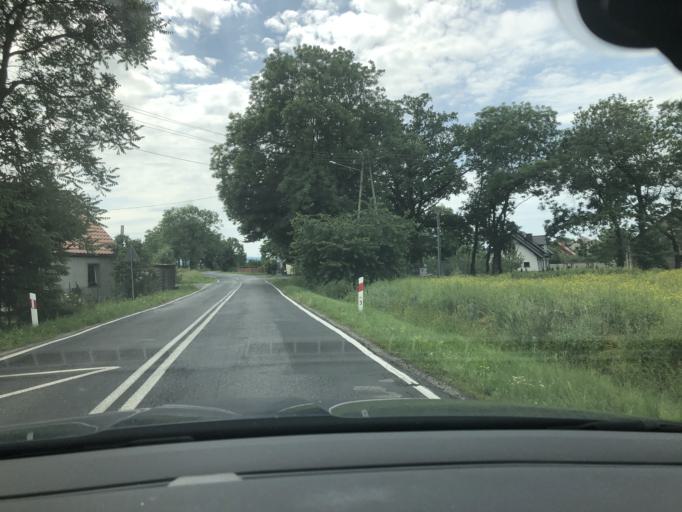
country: PL
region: Lower Silesian Voivodeship
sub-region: Powiat zlotoryjski
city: Zlotoryja
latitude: 51.1630
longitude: 15.9189
